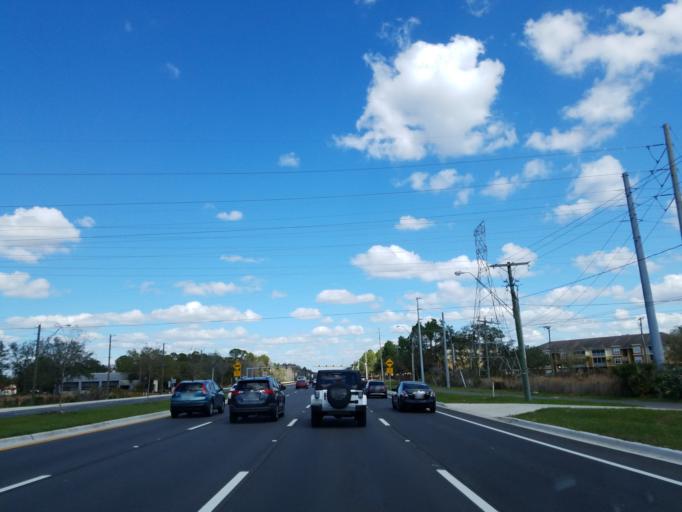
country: US
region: Florida
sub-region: Hillsborough County
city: University
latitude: 28.1046
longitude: -82.3915
